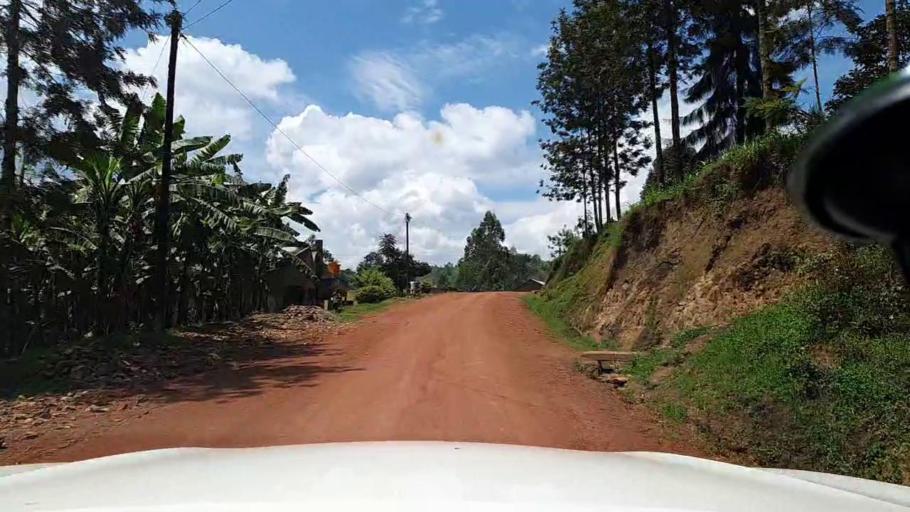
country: RW
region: Northern Province
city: Byumba
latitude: -1.7041
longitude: 29.8384
